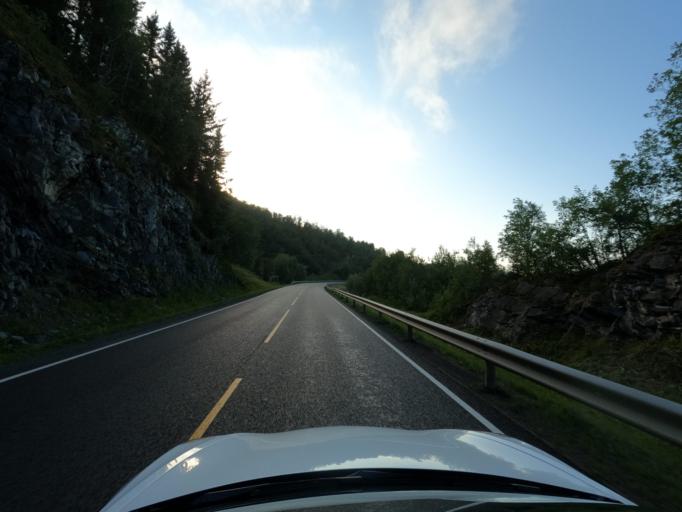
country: NO
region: Troms
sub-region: Skanland
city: Evenskjer
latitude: 68.6708
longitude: 16.5731
